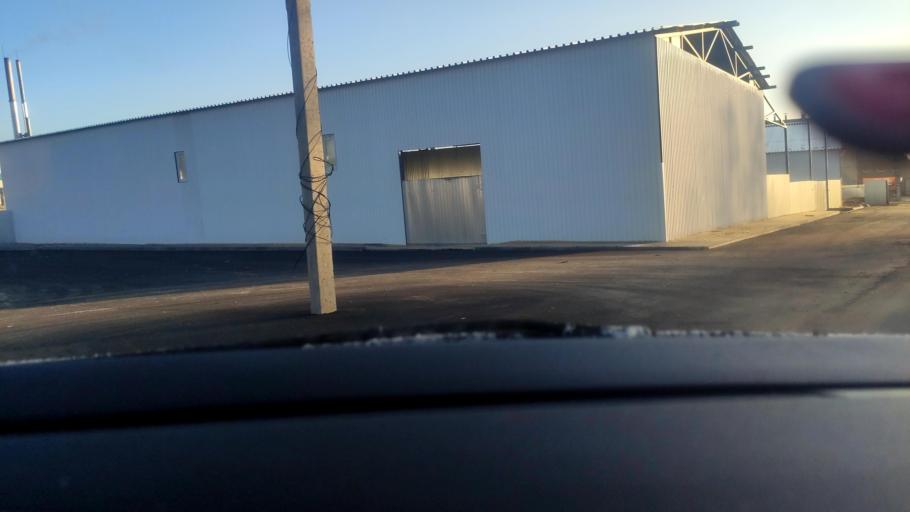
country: RU
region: Voronezj
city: Pridonskoy
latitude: 51.6402
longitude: 39.0967
